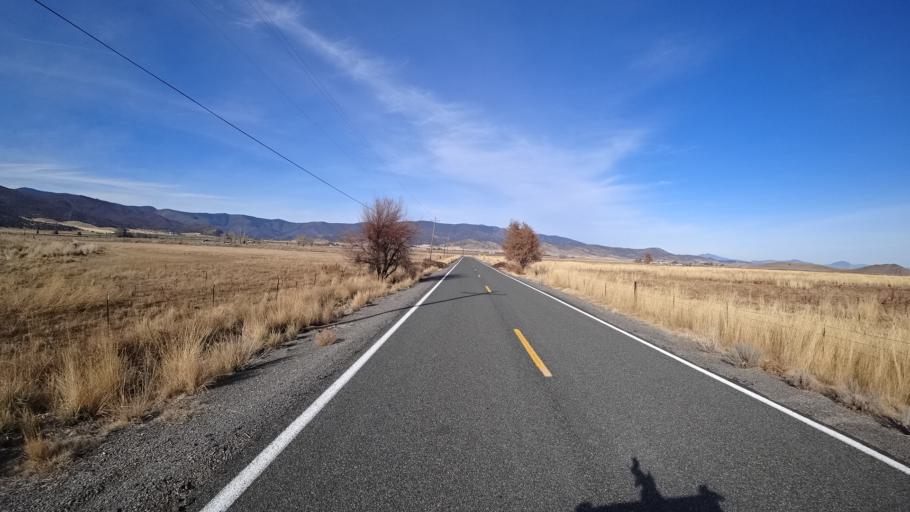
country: US
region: California
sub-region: Siskiyou County
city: Weed
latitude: 41.5366
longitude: -122.5211
